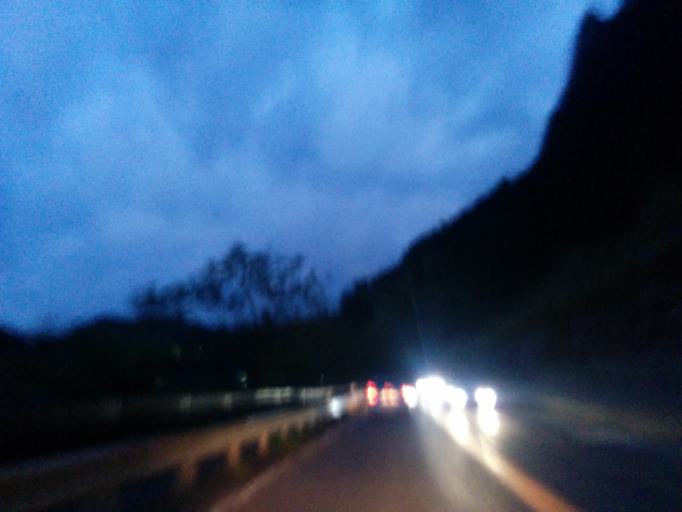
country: JP
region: Gifu
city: Mino
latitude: 35.5690
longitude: 136.9230
